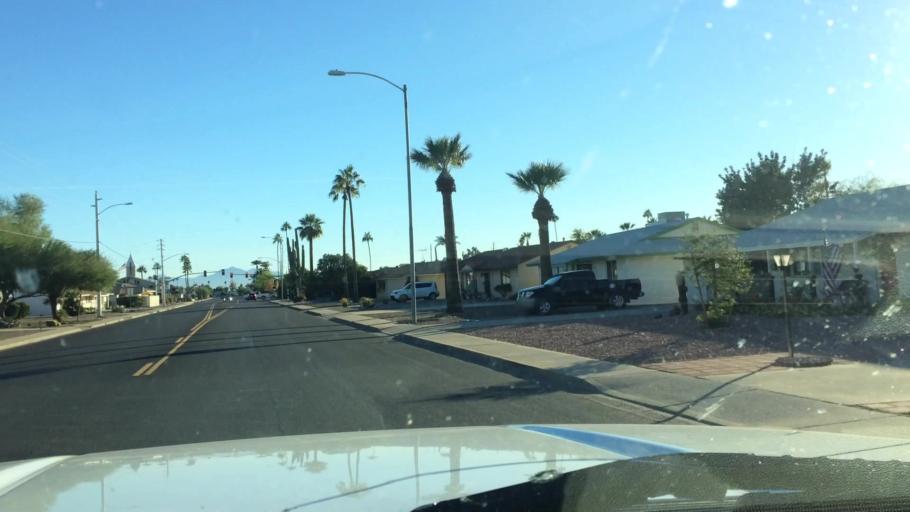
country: US
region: Arizona
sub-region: Maricopa County
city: Sun City
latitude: 33.5820
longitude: -112.2814
